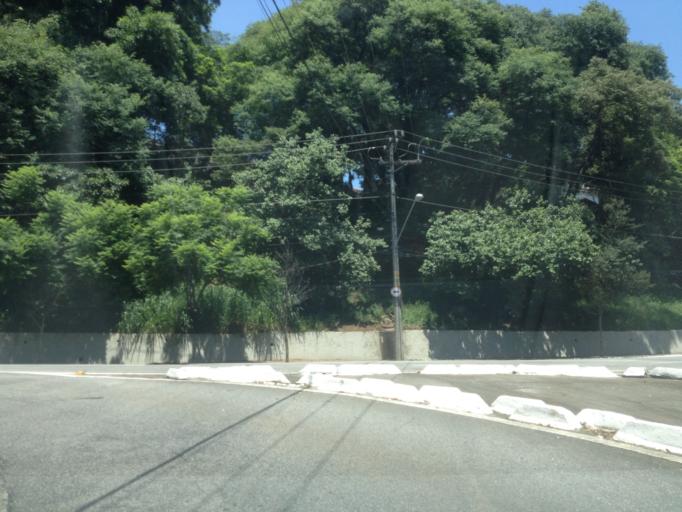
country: BR
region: Sao Paulo
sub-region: Sao Paulo
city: Sao Paulo
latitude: -23.5514
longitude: -46.6654
